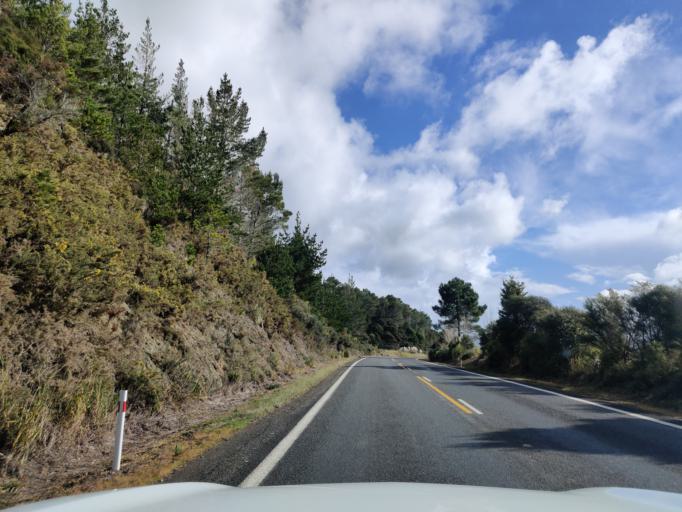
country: NZ
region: Waikato
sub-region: Thames-Coromandel District
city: Whitianga
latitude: -36.7483
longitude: 175.6735
